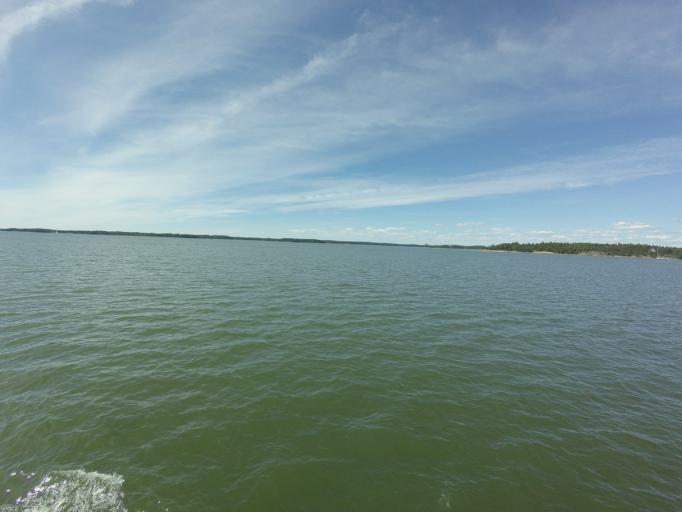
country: FI
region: Varsinais-Suomi
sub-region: Turku
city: Raisio
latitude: 60.3985
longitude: 22.1130
